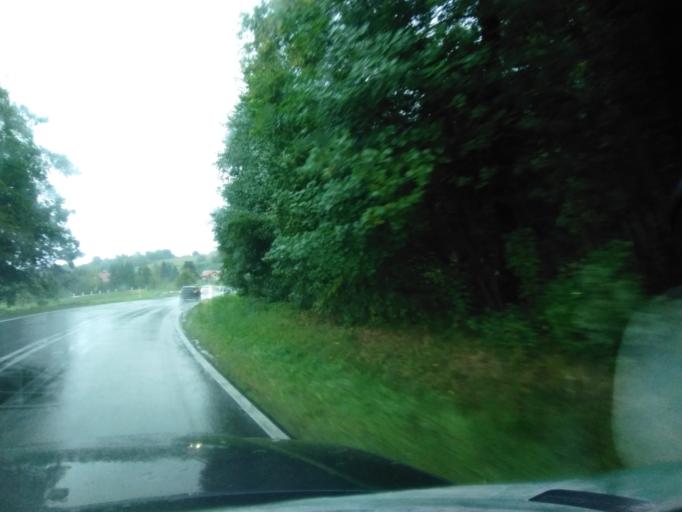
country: PL
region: Subcarpathian Voivodeship
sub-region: Powiat ropczycko-sedziszowski
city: Niedzwiada
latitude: 49.9895
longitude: 21.5623
